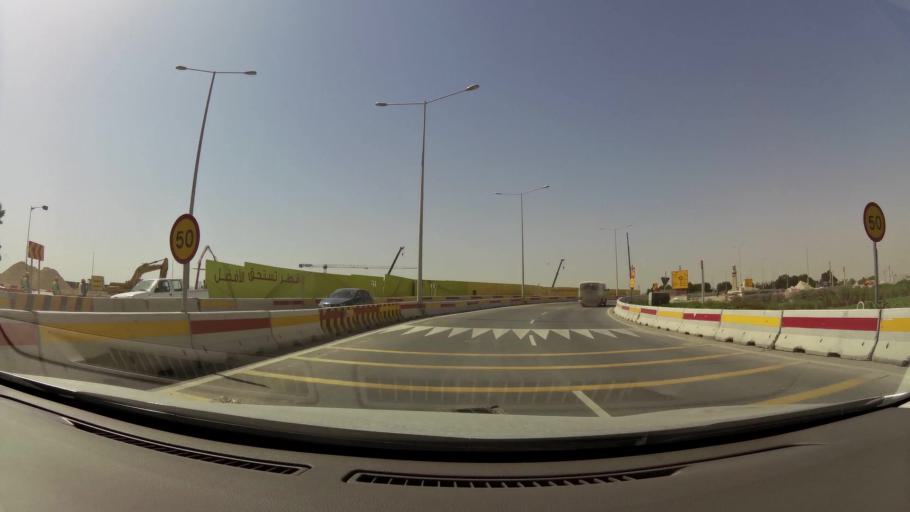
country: QA
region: Baladiyat ad Dawhah
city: Doha
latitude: 25.3743
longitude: 51.5254
